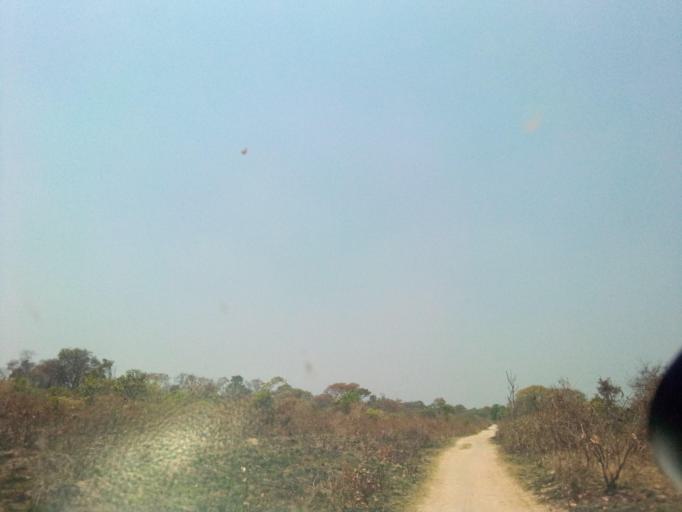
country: ZM
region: Copperbelt
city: Kataba
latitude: -12.2443
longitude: 30.3276
